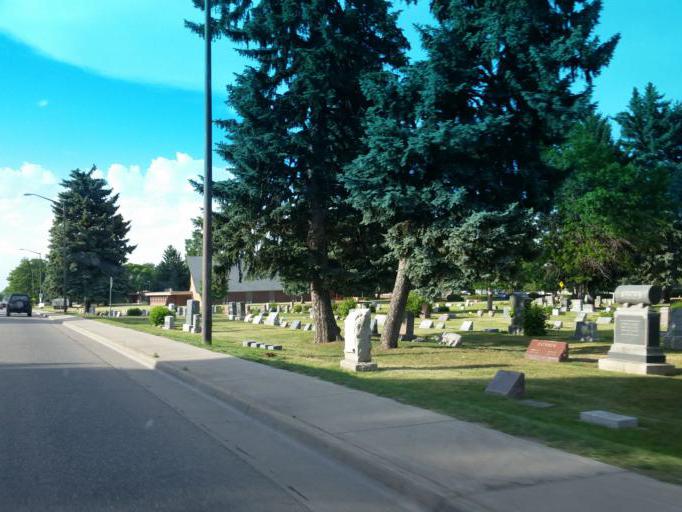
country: US
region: Colorado
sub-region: Larimer County
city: Loveland
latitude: 40.4118
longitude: -105.0730
